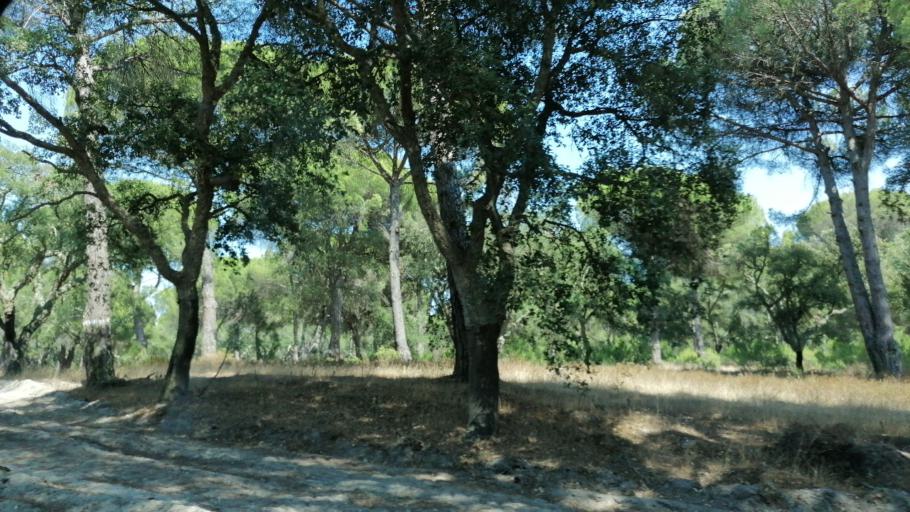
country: PT
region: Santarem
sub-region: Benavente
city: Poceirao
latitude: 38.7356
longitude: -8.6988
